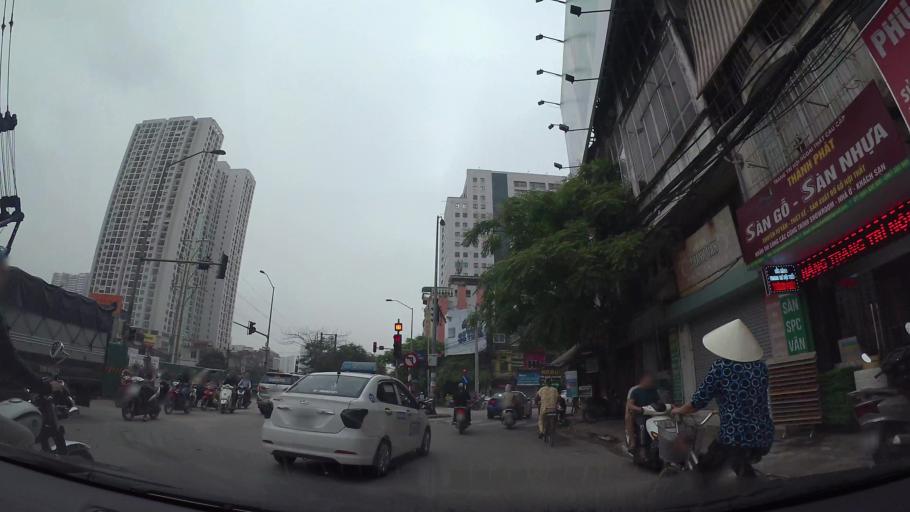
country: VN
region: Ha Noi
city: Hai BaTrung
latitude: 20.9965
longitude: 105.8619
